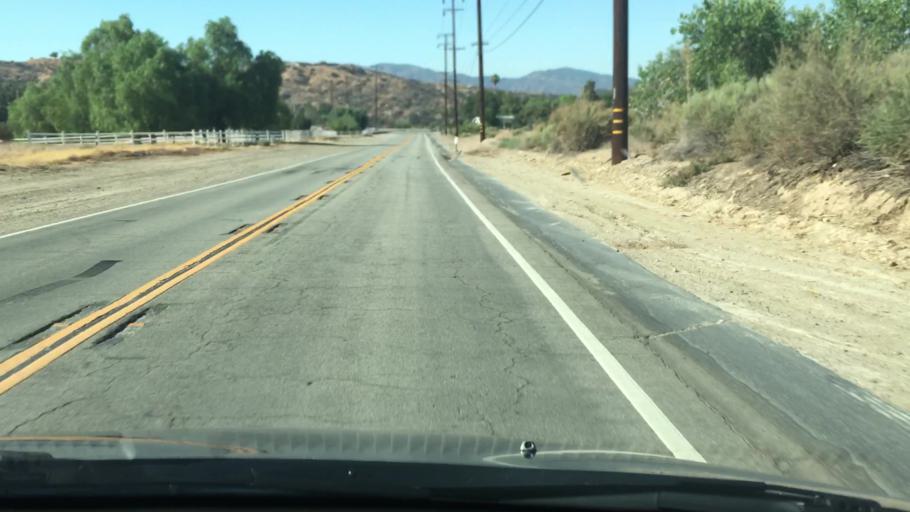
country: US
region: California
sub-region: Los Angeles County
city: Agua Dulce
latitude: 34.4587
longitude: -118.4212
